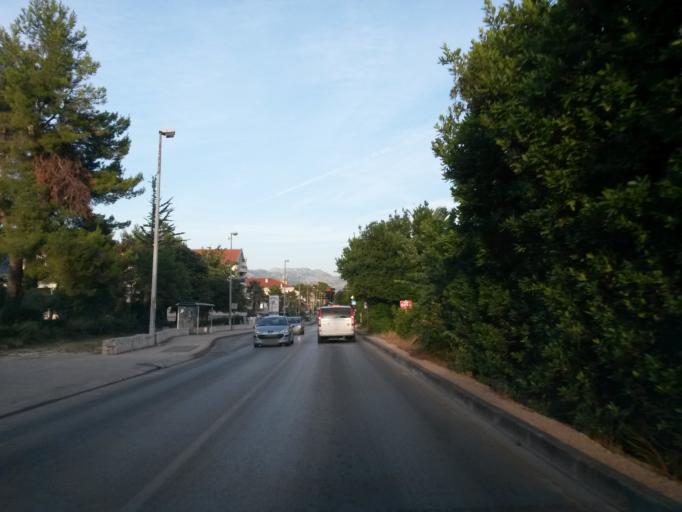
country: HR
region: Splitsko-Dalmatinska
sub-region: Grad Split
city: Split
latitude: 43.5496
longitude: 16.3912
